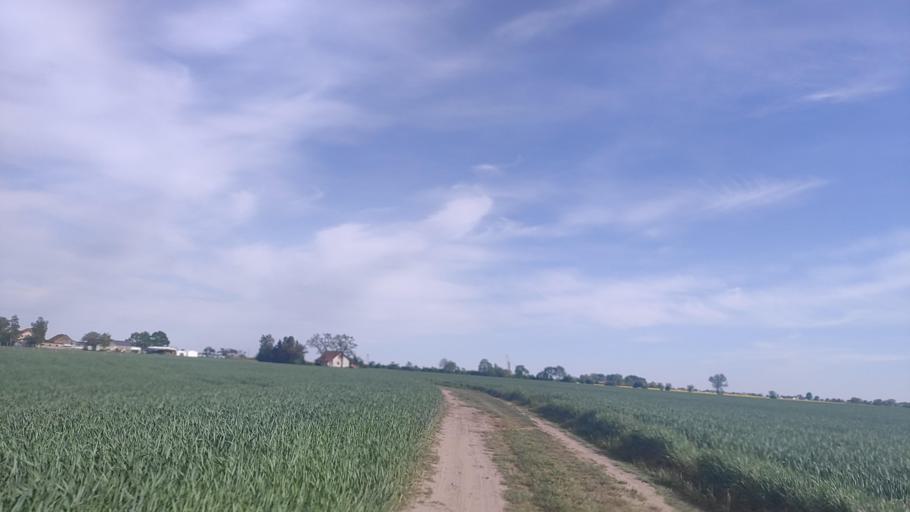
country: PL
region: Greater Poland Voivodeship
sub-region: Powiat poznanski
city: Swarzedz
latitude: 52.4162
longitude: 17.1486
